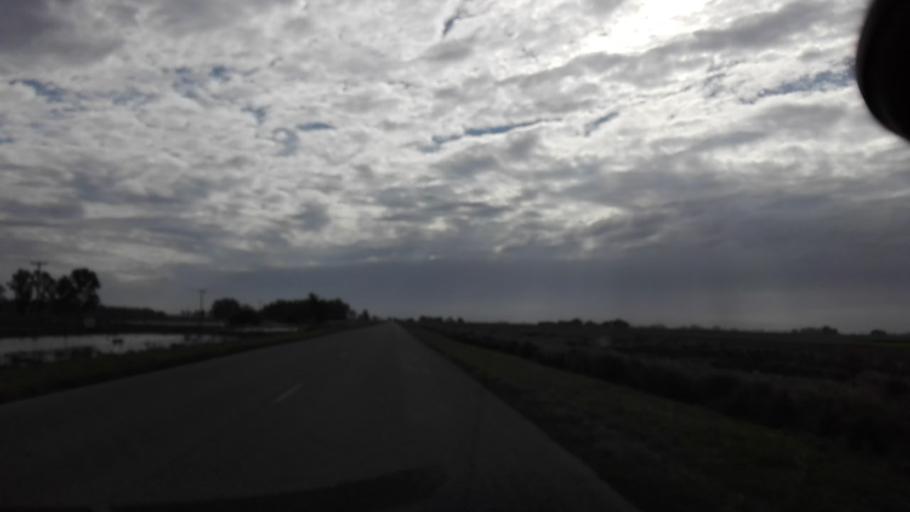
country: AR
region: Buenos Aires
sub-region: Partido de Las Flores
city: Las Flores
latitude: -36.1207
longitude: -59.0813
